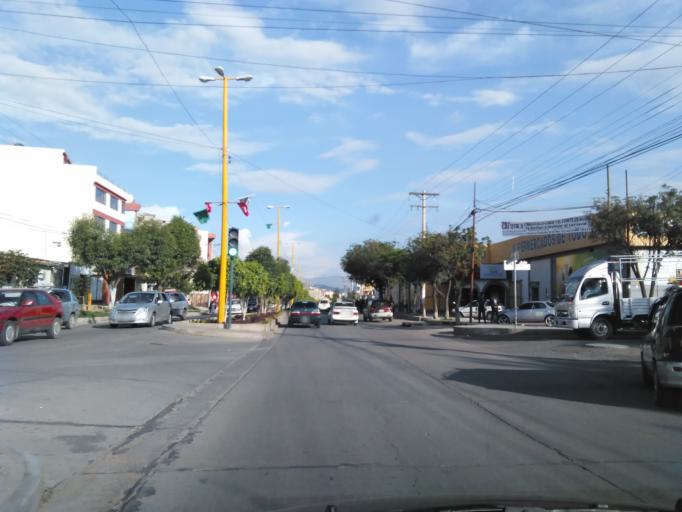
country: BO
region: Cochabamba
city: Cochabamba
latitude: -17.3506
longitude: -66.1931
